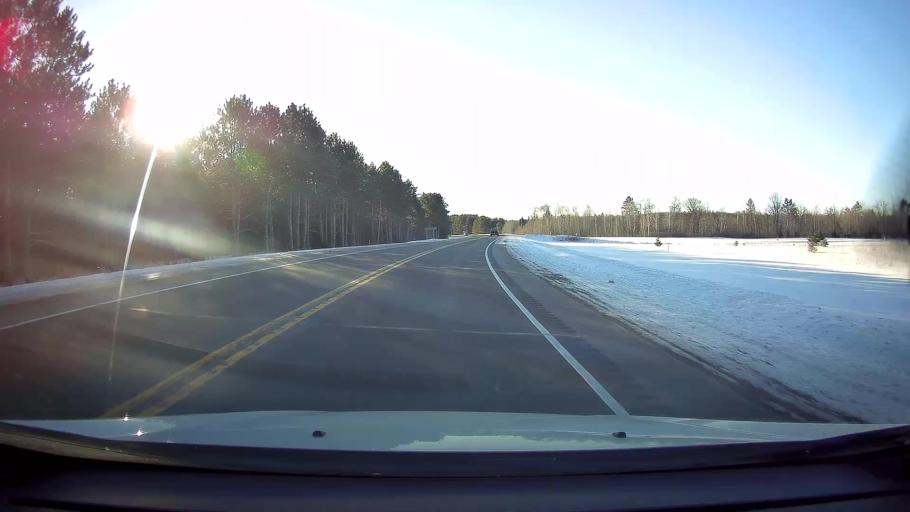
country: US
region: Wisconsin
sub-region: Sawyer County
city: Hayward
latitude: 45.9935
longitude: -91.5936
